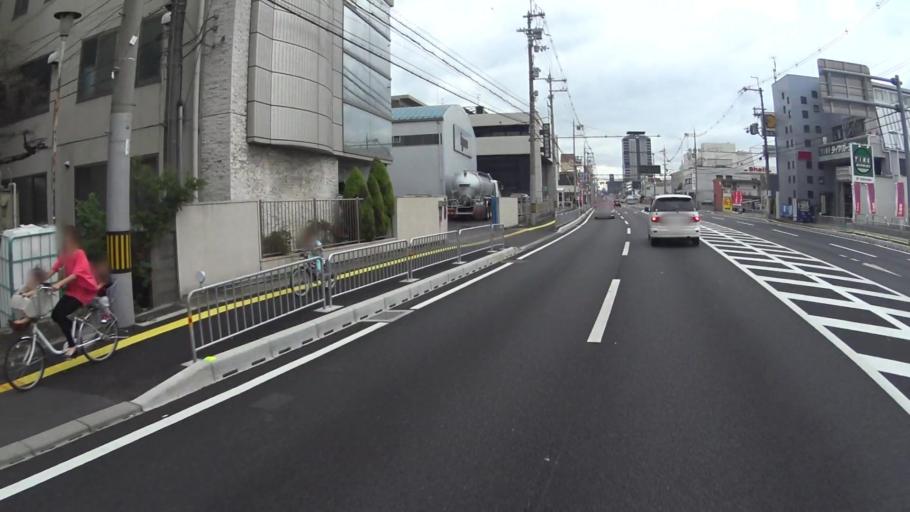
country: JP
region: Kyoto
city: Muko
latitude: 34.9588
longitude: 135.7170
